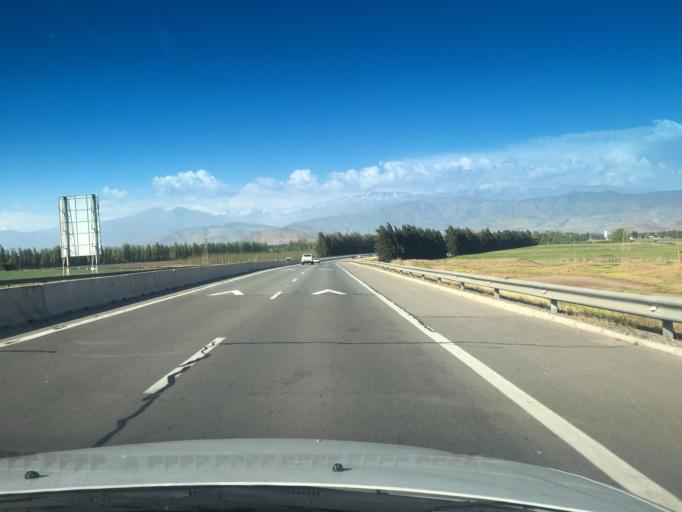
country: CL
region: Santiago Metropolitan
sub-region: Provincia de Chacabuco
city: Chicureo Abajo
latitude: -33.2964
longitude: -70.7226
